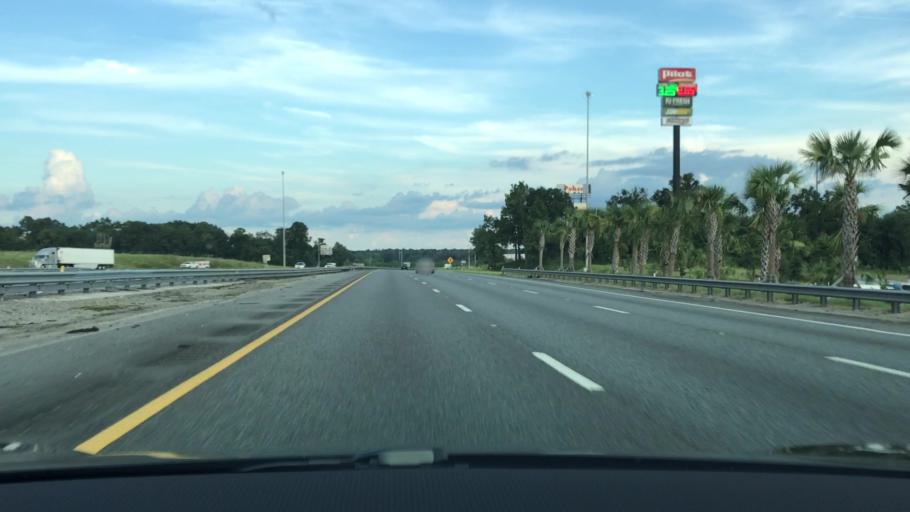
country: US
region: Florida
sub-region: Hamilton County
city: Jasper
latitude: 30.5183
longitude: -83.0574
